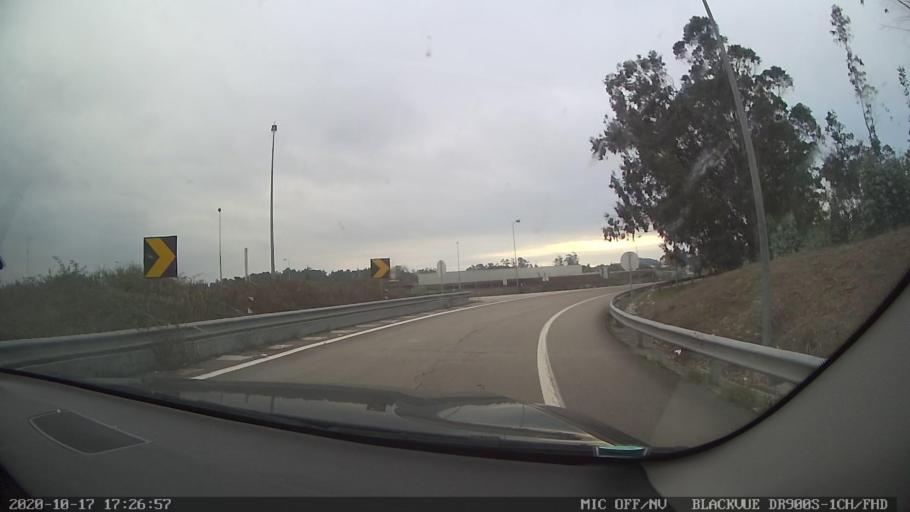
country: PT
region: Porto
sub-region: Vila do Conde
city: Vila do Conde
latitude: 41.3753
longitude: -8.7281
